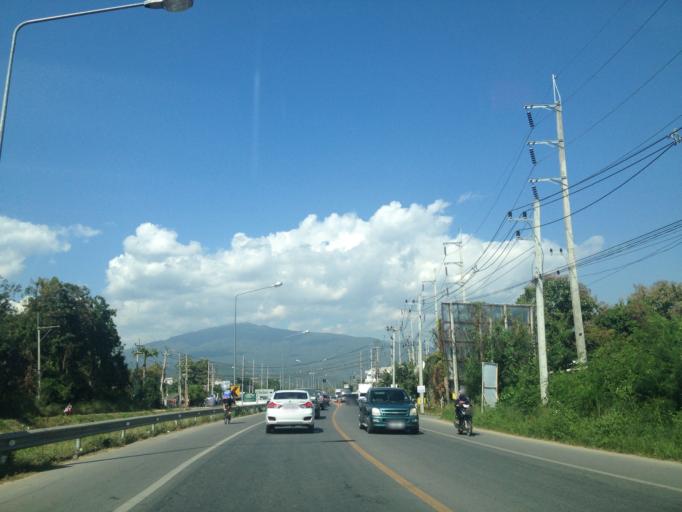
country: TH
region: Chiang Mai
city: Hang Dong
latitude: 18.7223
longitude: 98.9277
